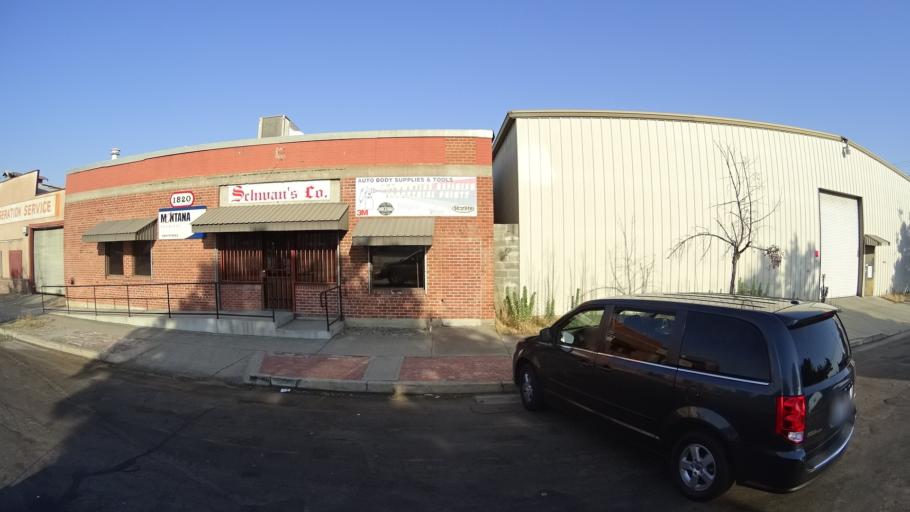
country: US
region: California
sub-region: Fresno County
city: Fresno
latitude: 36.7246
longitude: -119.7761
